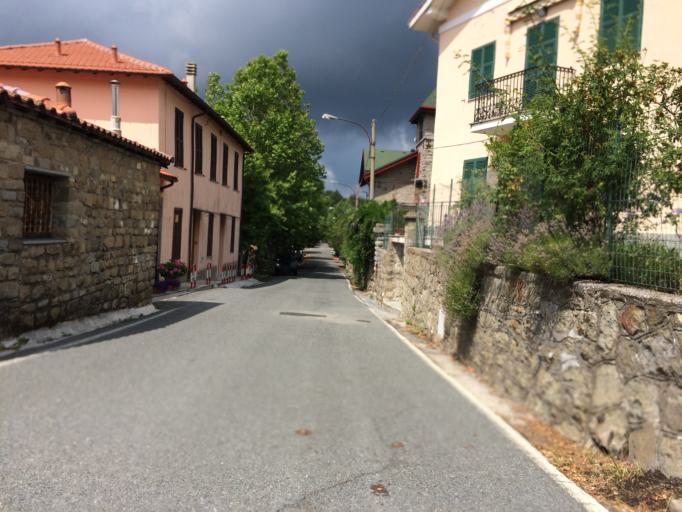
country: IT
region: Liguria
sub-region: Provincia di Imperia
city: Bajardo
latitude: 43.9033
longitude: 7.7223
